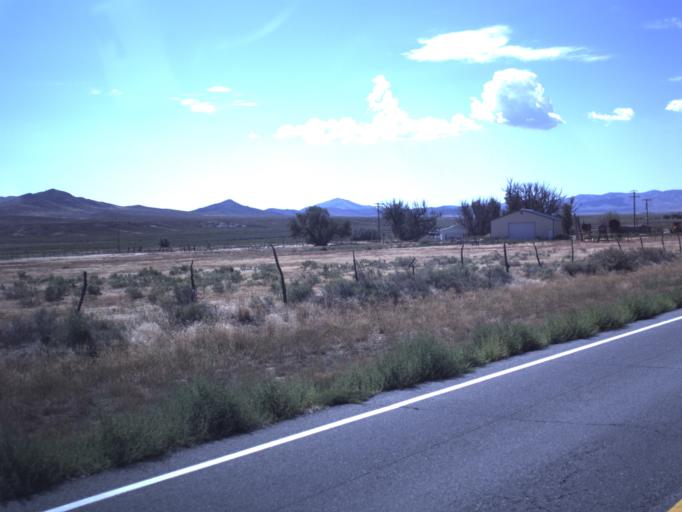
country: US
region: Utah
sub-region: Tooele County
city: Tooele
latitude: 40.1758
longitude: -112.4264
